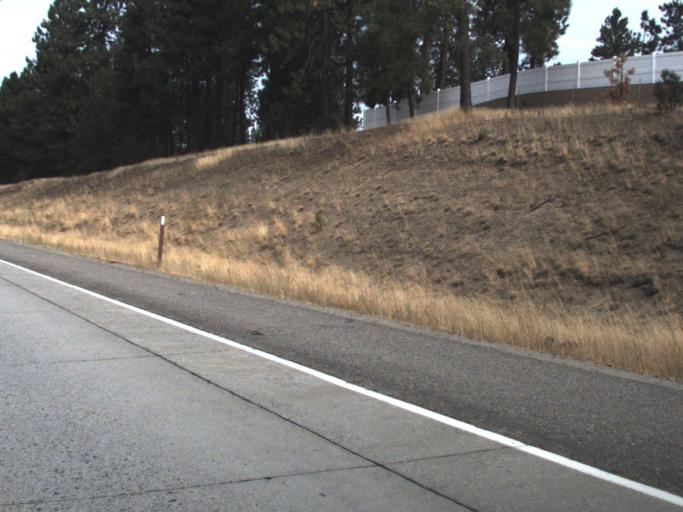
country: US
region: Washington
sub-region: Spokane County
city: Fairwood
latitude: 47.8121
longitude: -117.4073
